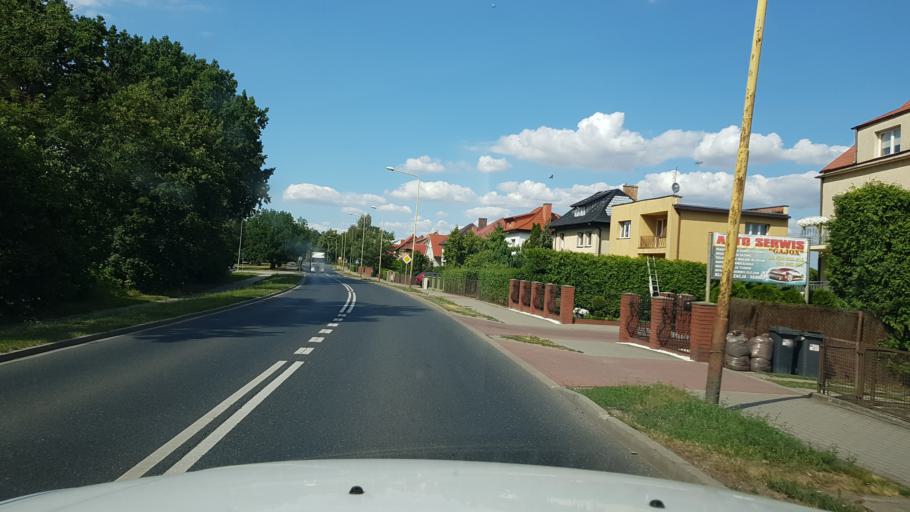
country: PL
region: West Pomeranian Voivodeship
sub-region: Powiat pyrzycki
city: Pyrzyce
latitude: 53.1345
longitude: 14.8930
